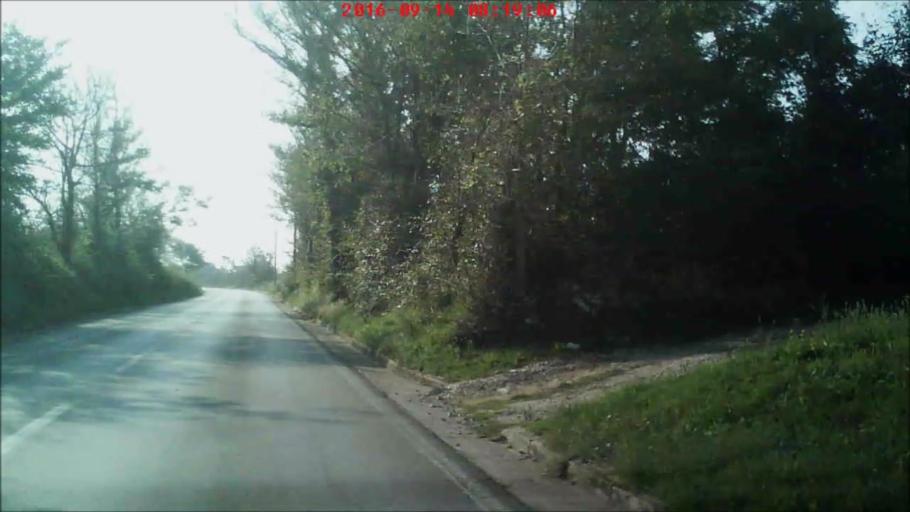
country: HR
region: Zadarska
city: Nin
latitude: 44.2350
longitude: 15.1873
